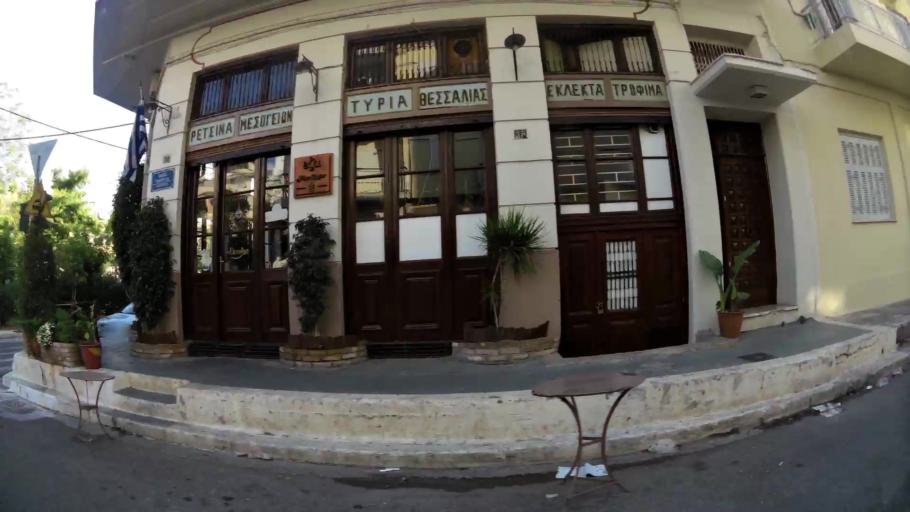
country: GR
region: Attica
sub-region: Nomos Attikis
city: Piraeus
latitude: 37.9535
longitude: 23.6338
